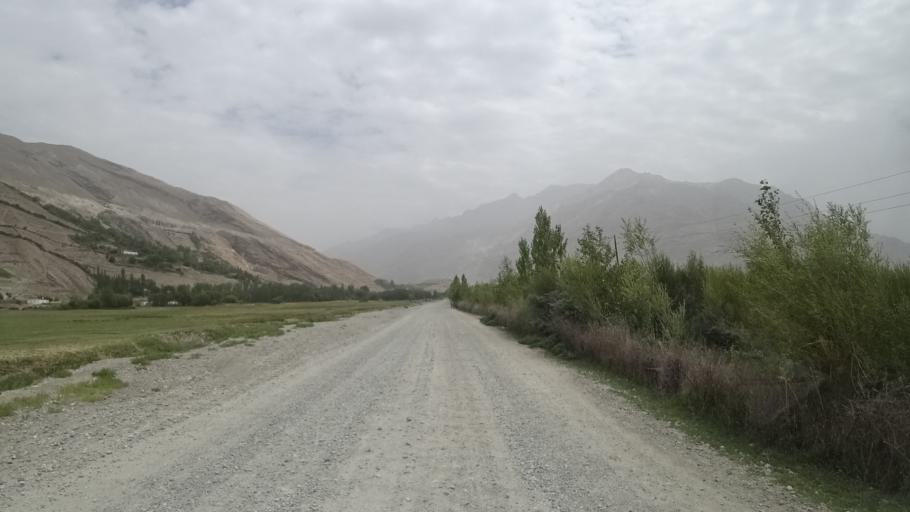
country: AF
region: Badakhshan
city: Khandud
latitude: 37.0349
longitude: 72.6394
